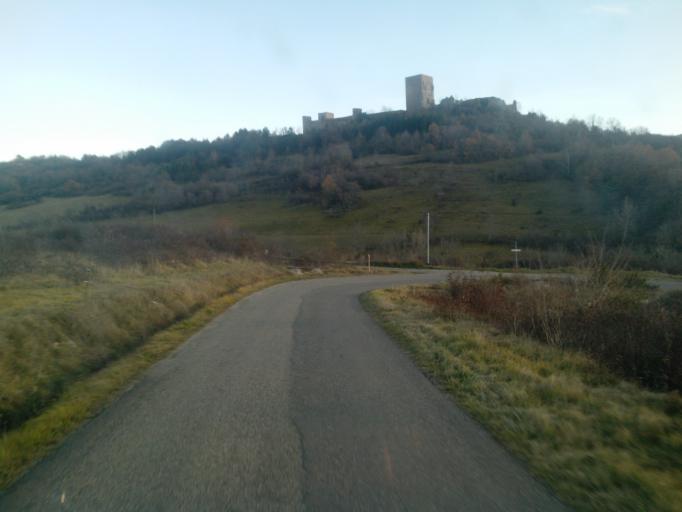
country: FR
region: Languedoc-Roussillon
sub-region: Departement de l'Aude
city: Chalabre
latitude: 42.9246
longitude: 2.0513
